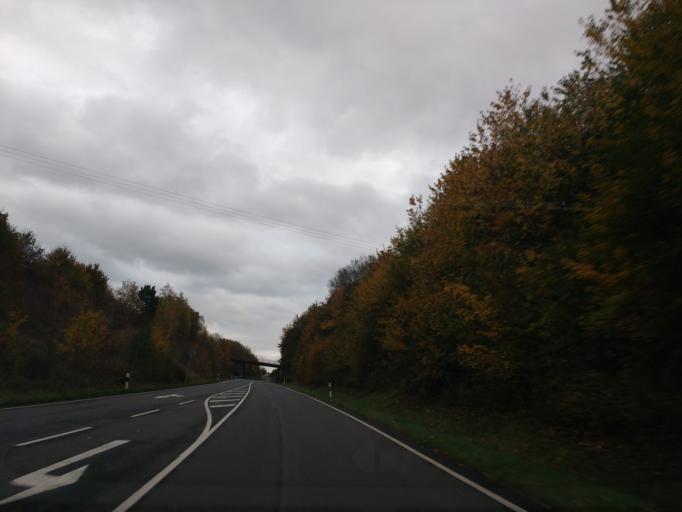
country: DE
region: Lower Saxony
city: Bad Lauterberg im Harz
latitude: 51.6006
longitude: 10.4548
